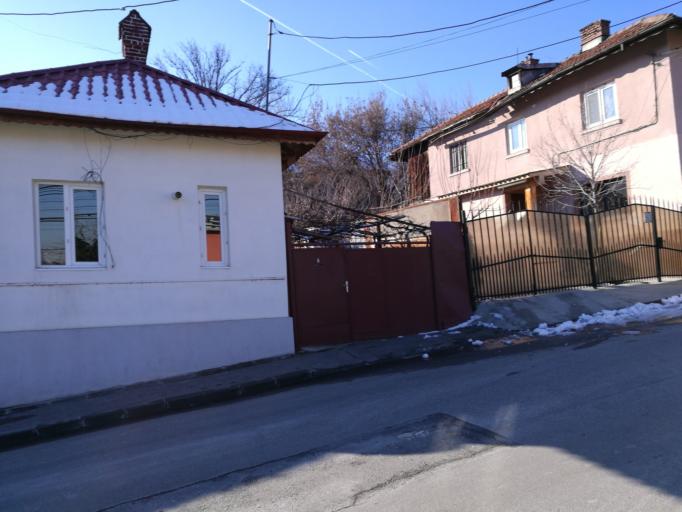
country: RO
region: Bucuresti
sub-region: Municipiul Bucuresti
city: Bucharest
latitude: 44.4760
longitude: 26.1109
